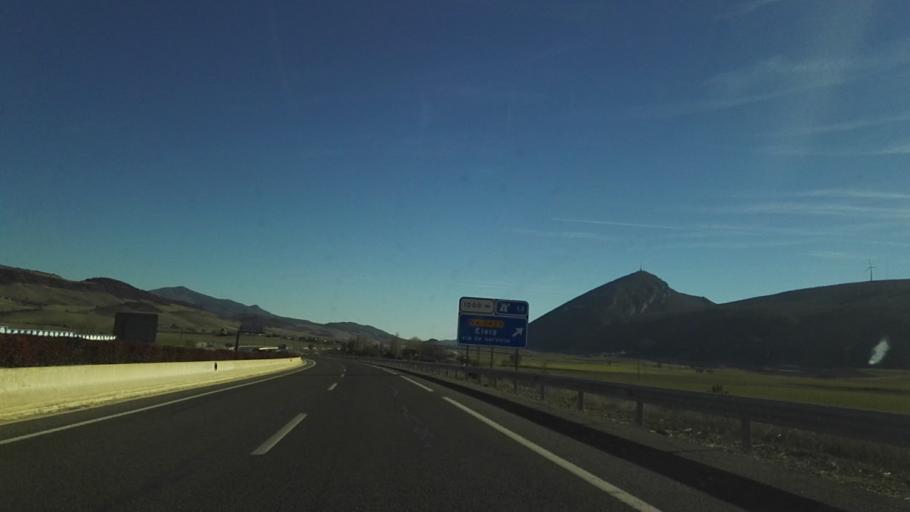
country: ES
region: Navarre
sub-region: Provincia de Navarra
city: Elorz
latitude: 42.7392
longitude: -1.5836
